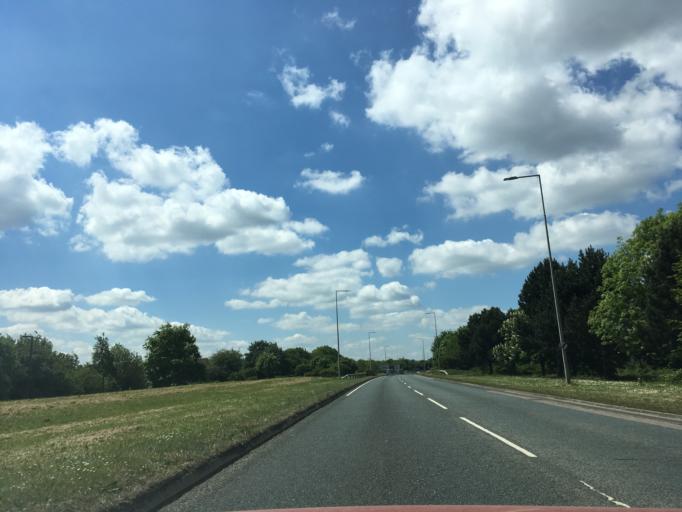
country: GB
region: England
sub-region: Milton Keynes
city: Broughton
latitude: 52.0381
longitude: -0.7037
